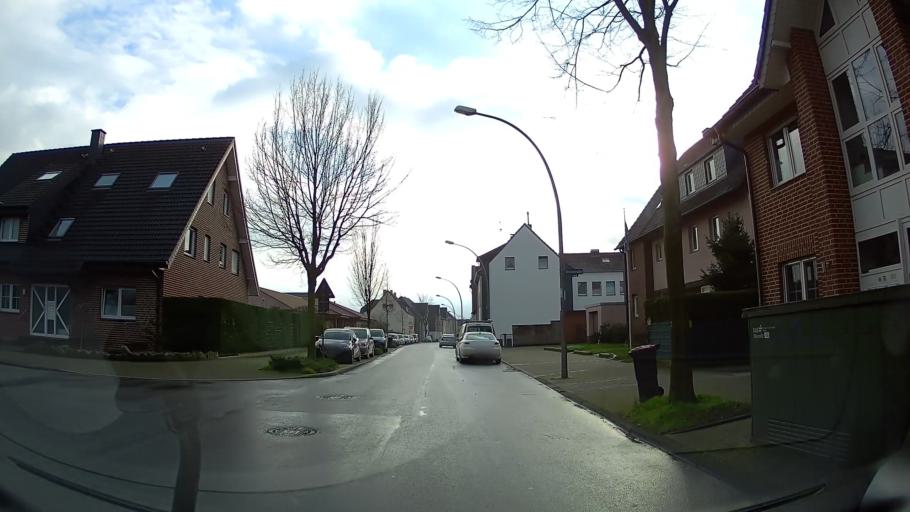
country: DE
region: North Rhine-Westphalia
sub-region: Regierungsbezirk Munster
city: Gladbeck
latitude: 51.5612
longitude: 6.9926
